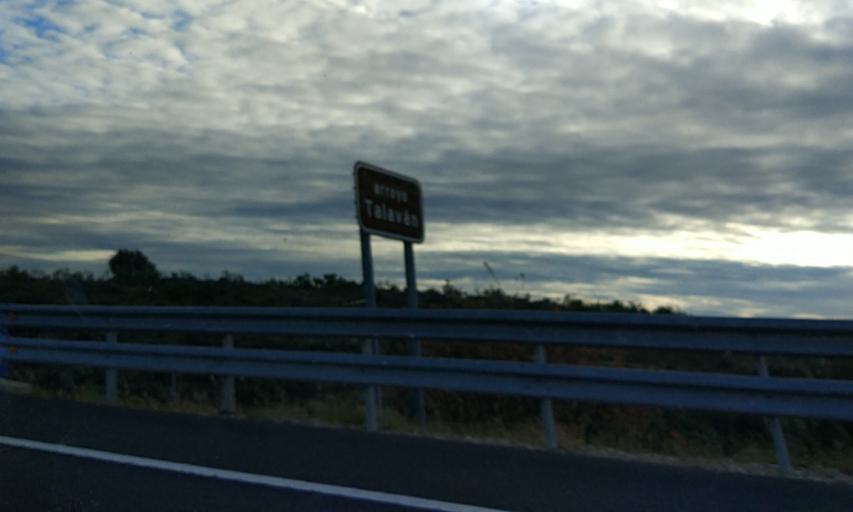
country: ES
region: Extremadura
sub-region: Provincia de Caceres
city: Hinojal
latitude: 39.6763
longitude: -6.3988
